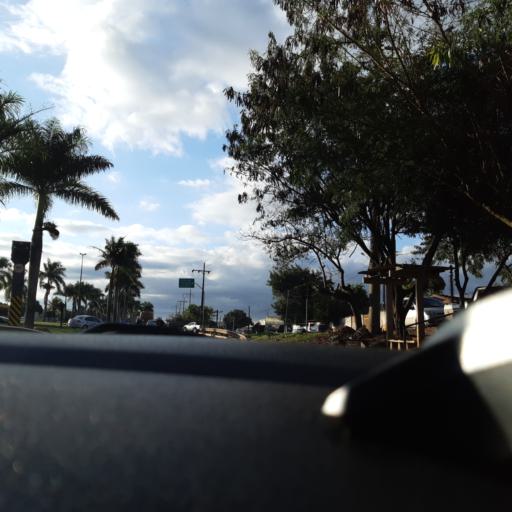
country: BR
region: Sao Paulo
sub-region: Ourinhos
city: Ourinhos
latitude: -22.9856
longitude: -49.8557
